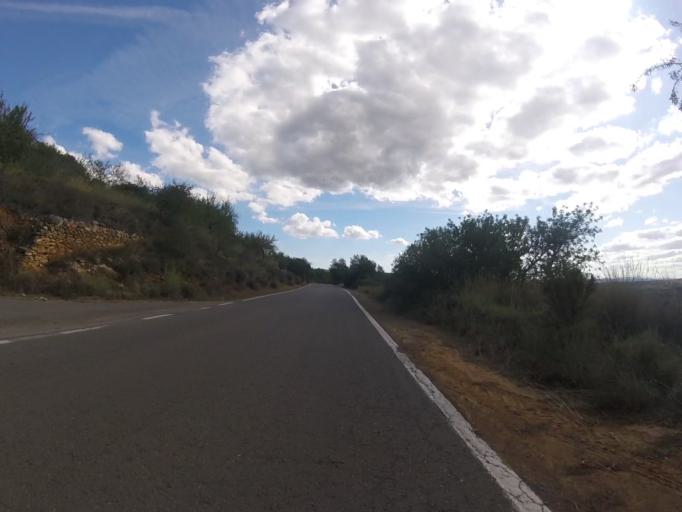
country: ES
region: Valencia
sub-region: Provincia de Castello
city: Cuevas de Vinroma
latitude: 40.3643
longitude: 0.1218
